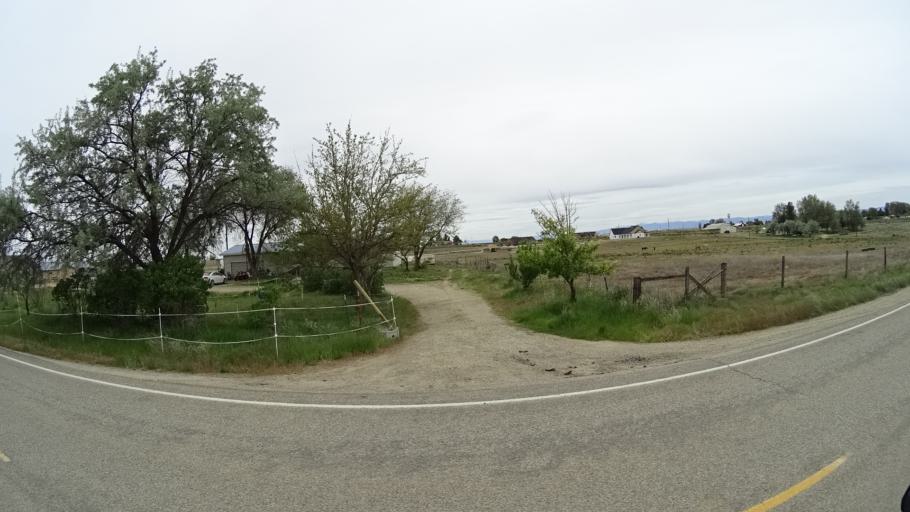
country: US
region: Idaho
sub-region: Ada County
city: Kuna
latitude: 43.4884
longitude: -116.3074
